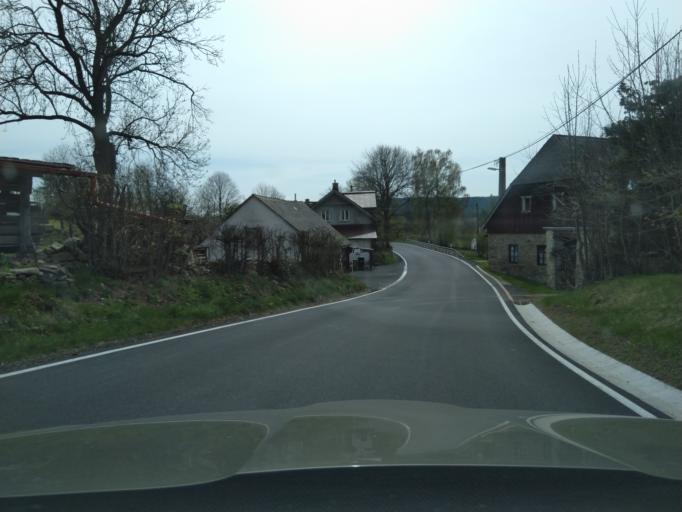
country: CZ
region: Jihocesky
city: Vacov
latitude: 49.1166
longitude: 13.7465
